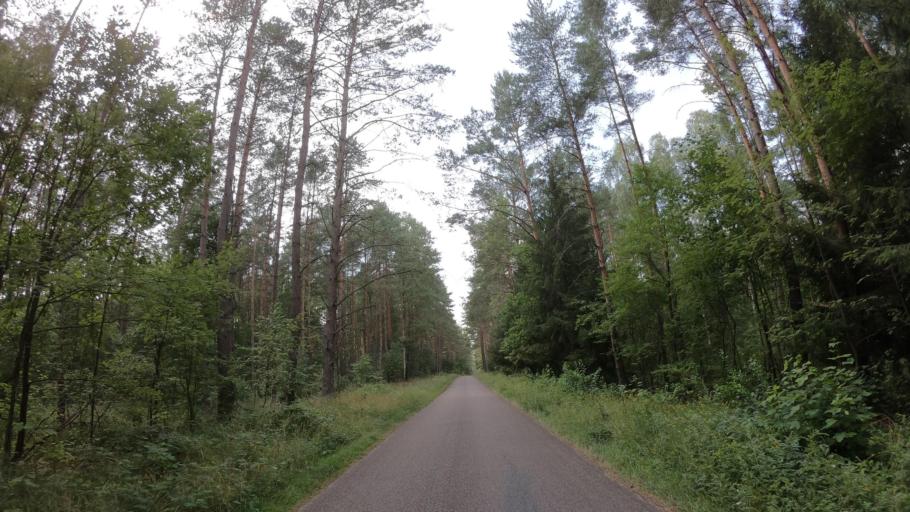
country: PL
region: West Pomeranian Voivodeship
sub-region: Powiat walecki
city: Tuczno
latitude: 53.2306
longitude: 16.0986
